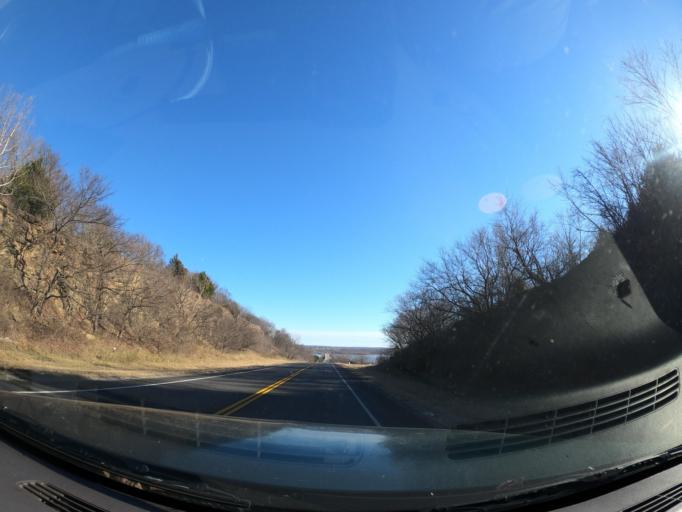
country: US
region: Oklahoma
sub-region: McIntosh County
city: Eufaula
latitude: 35.2517
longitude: -95.5726
